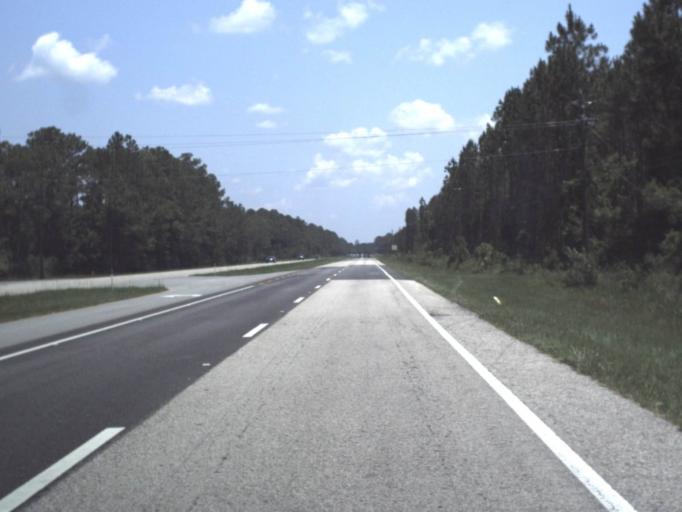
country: US
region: Florida
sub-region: Saint Johns County
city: Butler Beach
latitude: 29.7127
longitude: -81.3018
